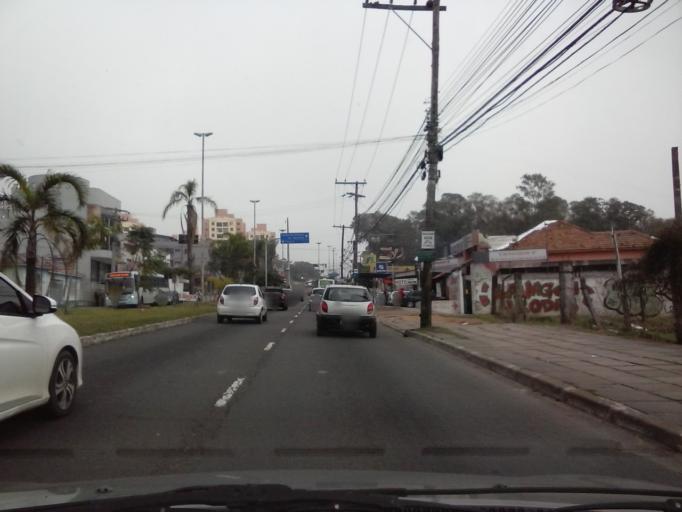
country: BR
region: Rio Grande do Sul
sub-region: Porto Alegre
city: Porto Alegre
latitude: -30.0423
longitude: -51.1345
